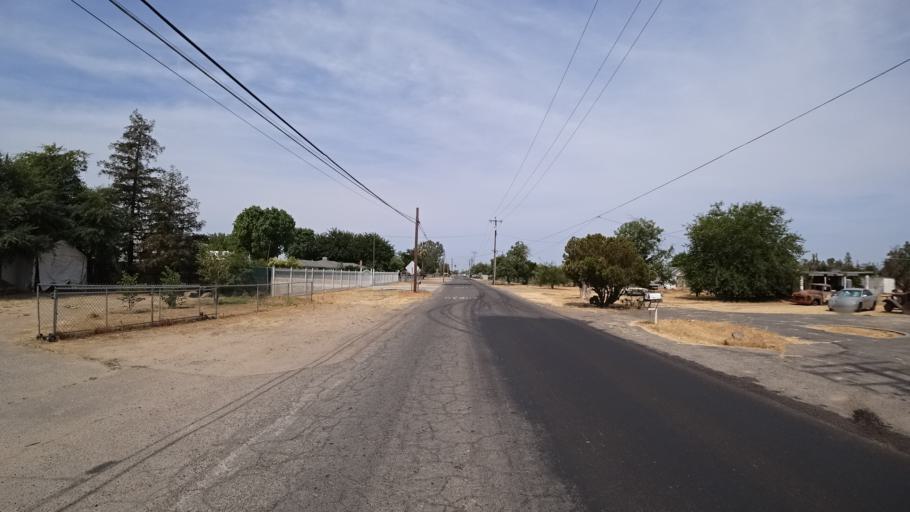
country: US
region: California
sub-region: Fresno County
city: West Park
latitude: 36.7573
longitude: -119.8819
